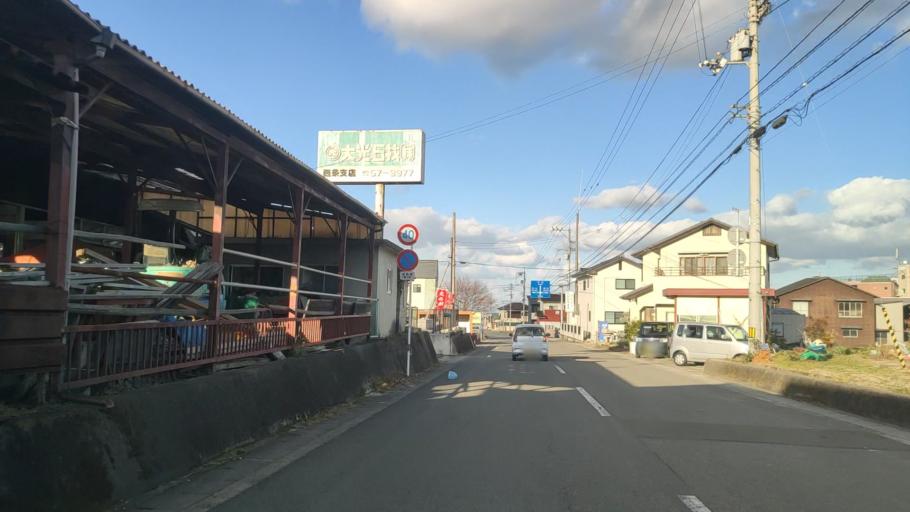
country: JP
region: Ehime
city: Saijo
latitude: 33.8927
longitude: 133.1319
